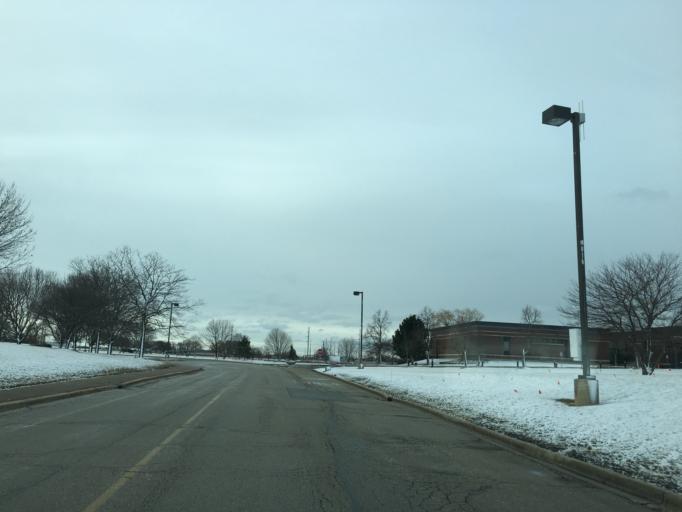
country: US
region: Illinois
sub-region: Cook County
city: Hoffman Estates
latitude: 42.0647
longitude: -88.0540
